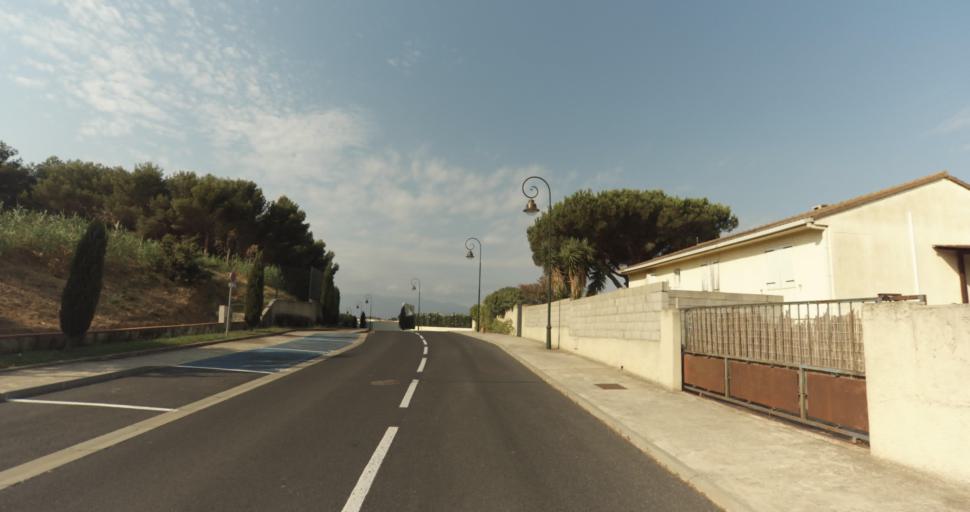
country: FR
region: Languedoc-Roussillon
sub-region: Departement des Pyrenees-Orientales
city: Latour-Bas-Elne
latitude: 42.6144
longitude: 2.9972
